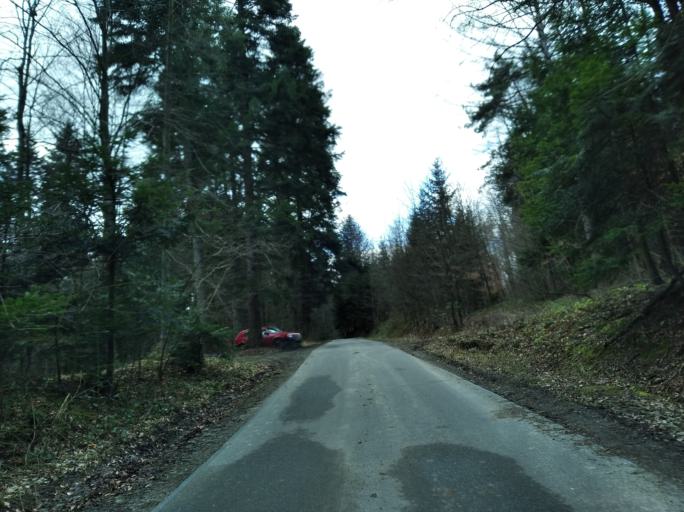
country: PL
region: Subcarpathian Voivodeship
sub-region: Powiat strzyzowski
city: Wysoka Strzyzowska
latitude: 49.7995
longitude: 21.7353
